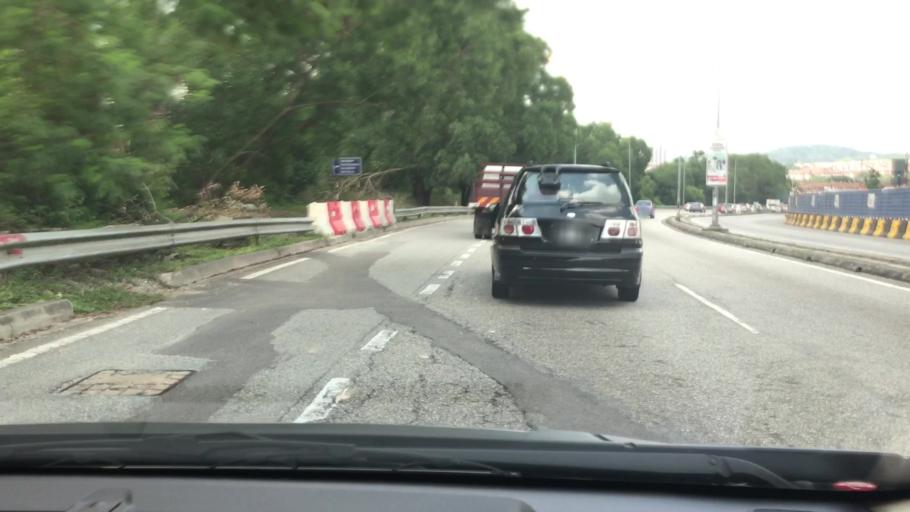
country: MY
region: Putrajaya
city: Putrajaya
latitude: 2.9841
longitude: 101.6616
